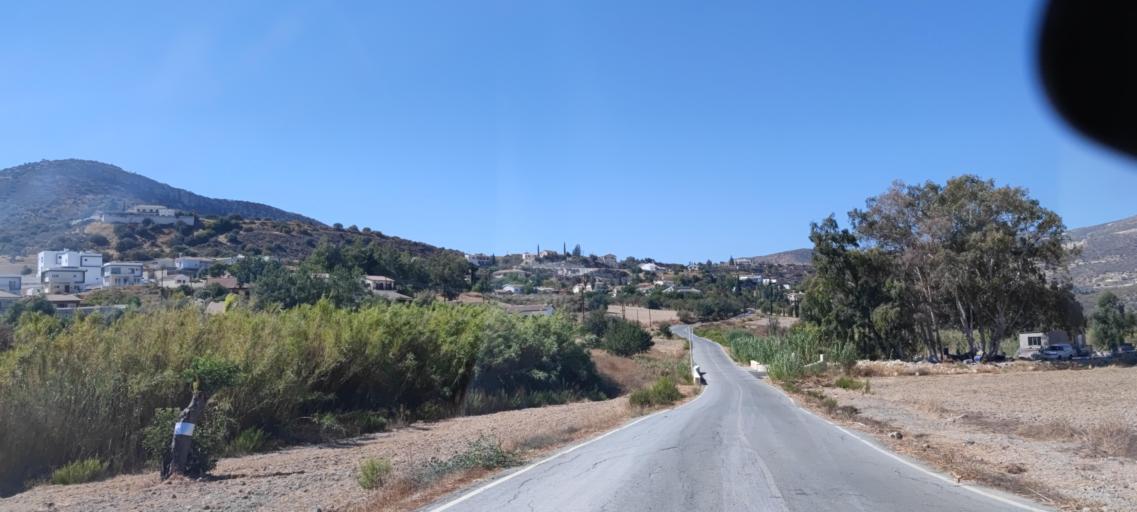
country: CY
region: Limassol
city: Mouttagiaka
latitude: 34.7540
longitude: 33.1064
